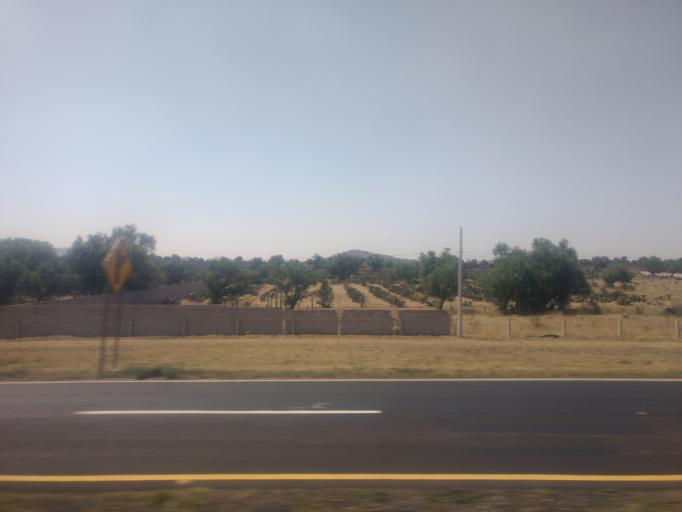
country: MX
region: Morelos
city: Nopaltepec
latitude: 19.7900
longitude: -98.7316
